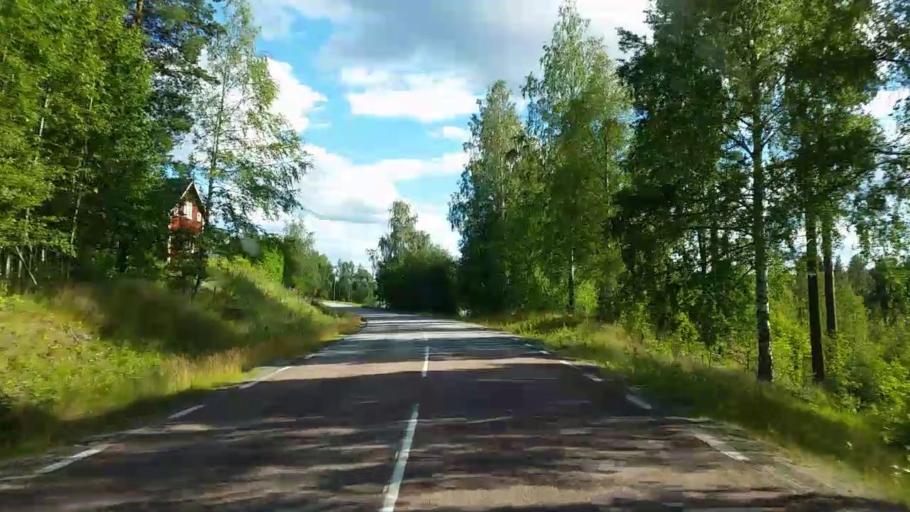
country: SE
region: Vaesternorrland
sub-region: Ange Kommun
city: Ange
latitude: 62.1566
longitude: 15.6768
